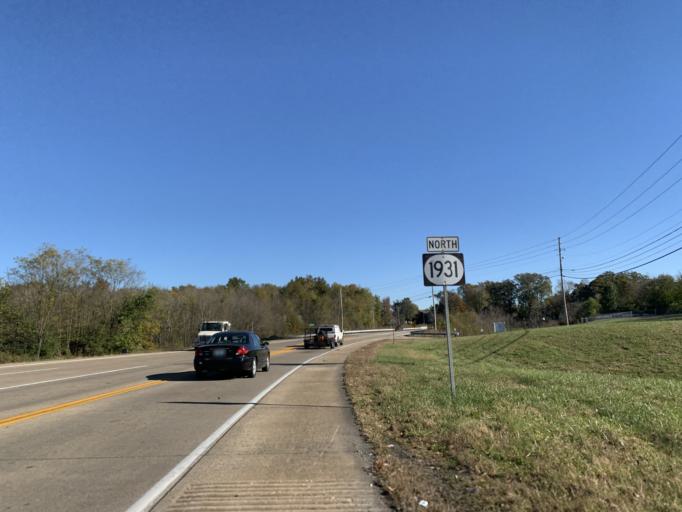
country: US
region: Kentucky
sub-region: Jefferson County
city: Pleasure Ridge Park
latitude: 38.1468
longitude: -85.8858
